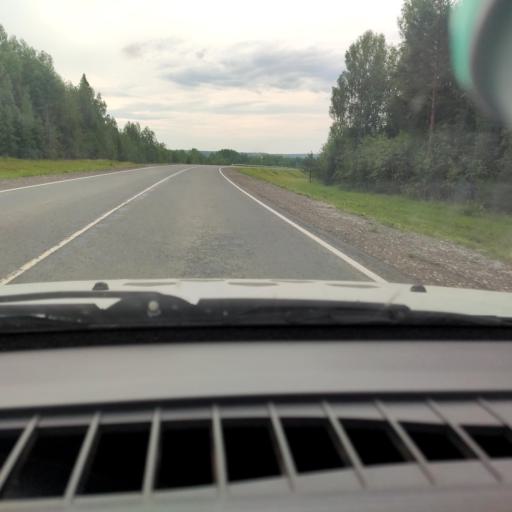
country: RU
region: Kirov
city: Kostino
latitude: 58.8131
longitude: 53.5913
